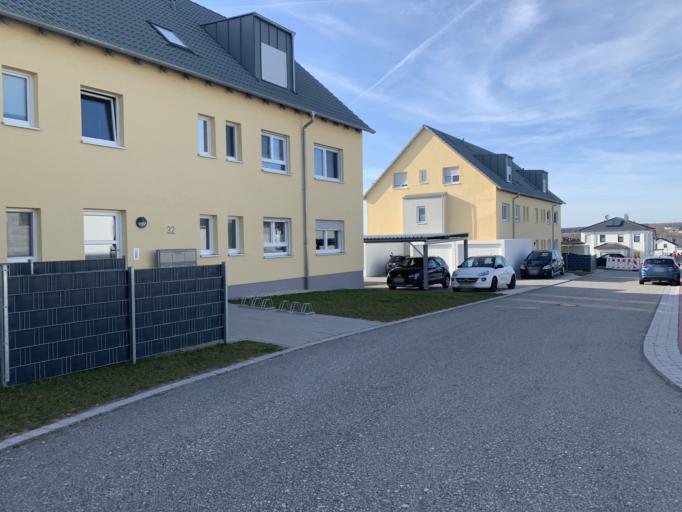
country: DE
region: Bavaria
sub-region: Regierungsbezirk Mittelfranken
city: Wilhermsdorf
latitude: 49.4731
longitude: 10.7224
